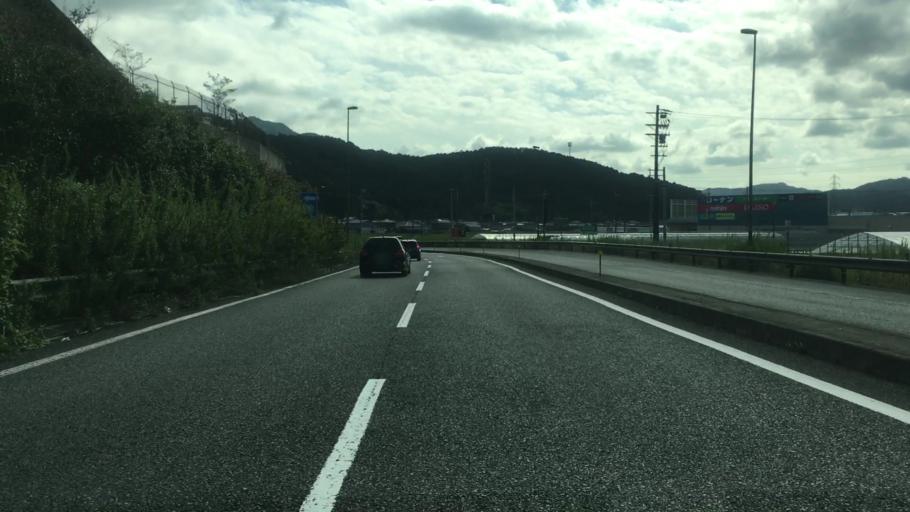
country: JP
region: Kyoto
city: Fukuchiyama
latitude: 35.1609
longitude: 135.0461
